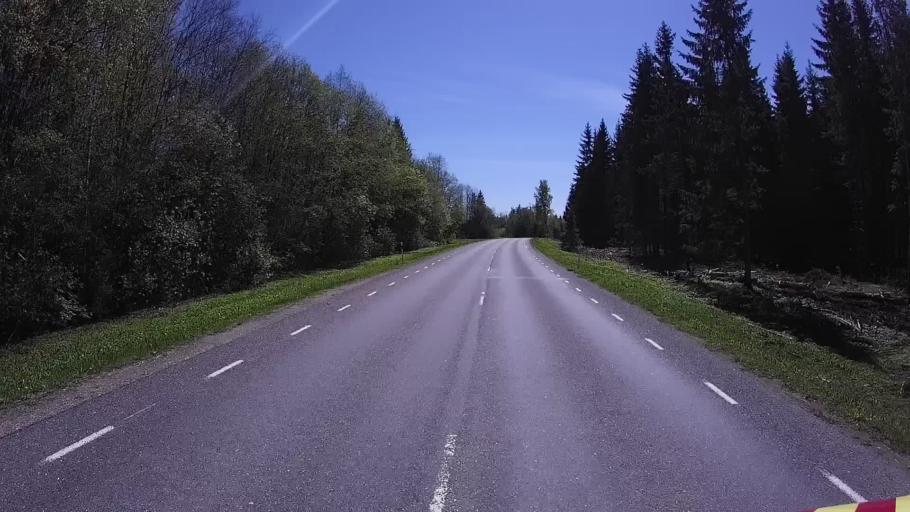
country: EE
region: Raplamaa
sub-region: Kehtna vald
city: Kehtna
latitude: 59.0494
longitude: 25.0234
